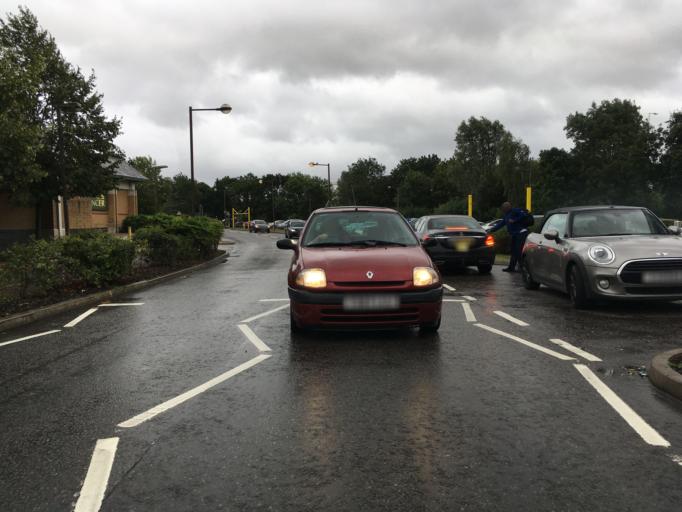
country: GB
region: England
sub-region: Milton Keynes
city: Broughton
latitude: 52.0346
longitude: -0.6898
